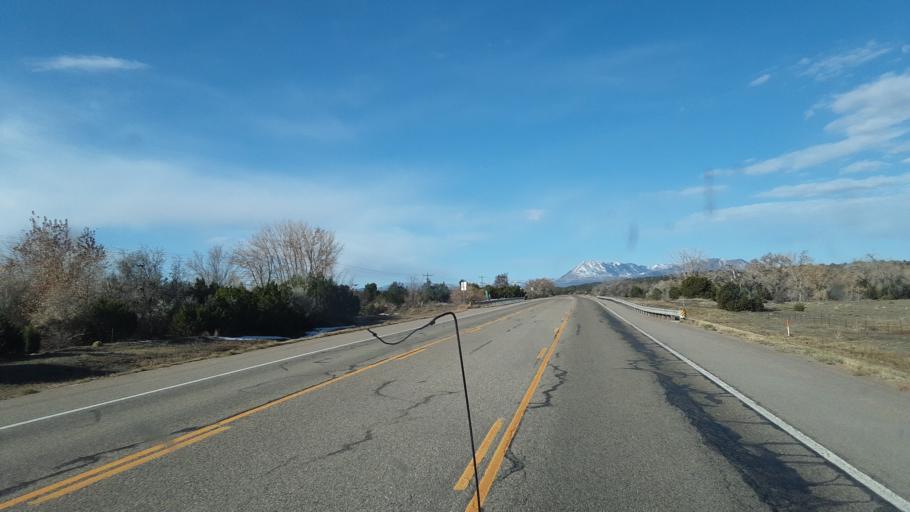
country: US
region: Colorado
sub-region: Huerfano County
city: Walsenburg
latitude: 37.5984
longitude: -104.8508
